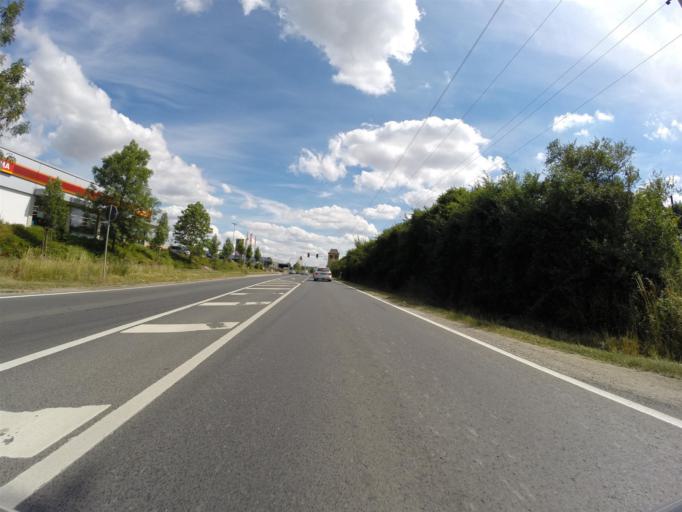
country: DE
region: Bavaria
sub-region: Regierungsbezirk Unterfranken
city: Volkach
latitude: 49.8625
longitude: 10.2240
